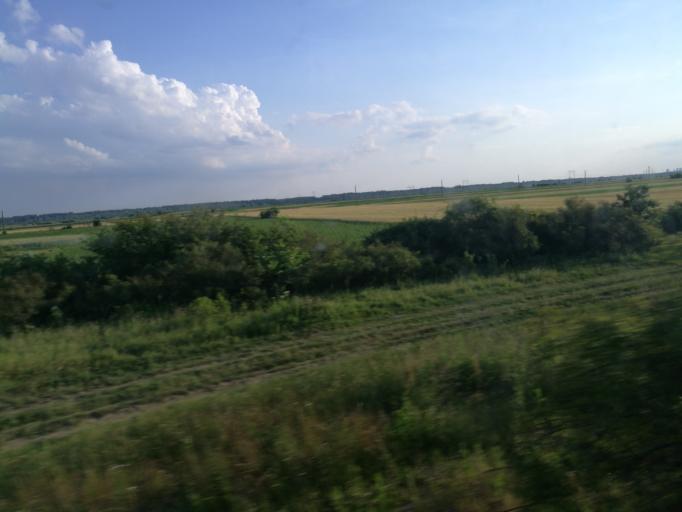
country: RO
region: Arges
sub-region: Comuna Calinesti
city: Calinesti
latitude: 44.8154
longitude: 25.0469
